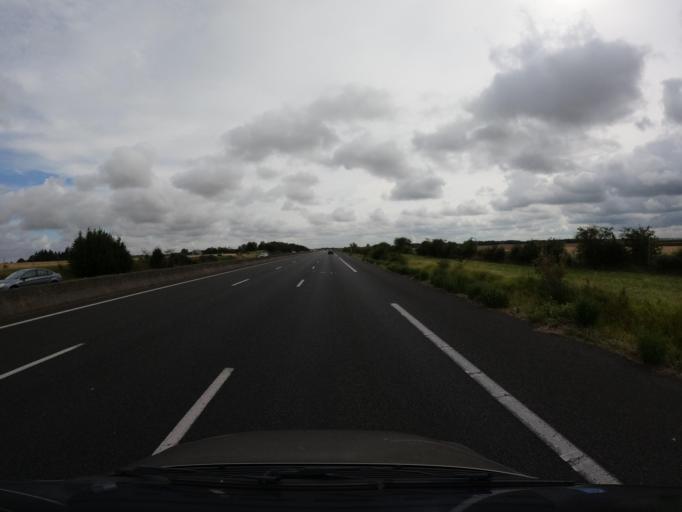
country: FR
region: Centre
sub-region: Departement du Loir-et-Cher
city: Suevres
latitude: 47.6866
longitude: 1.4226
